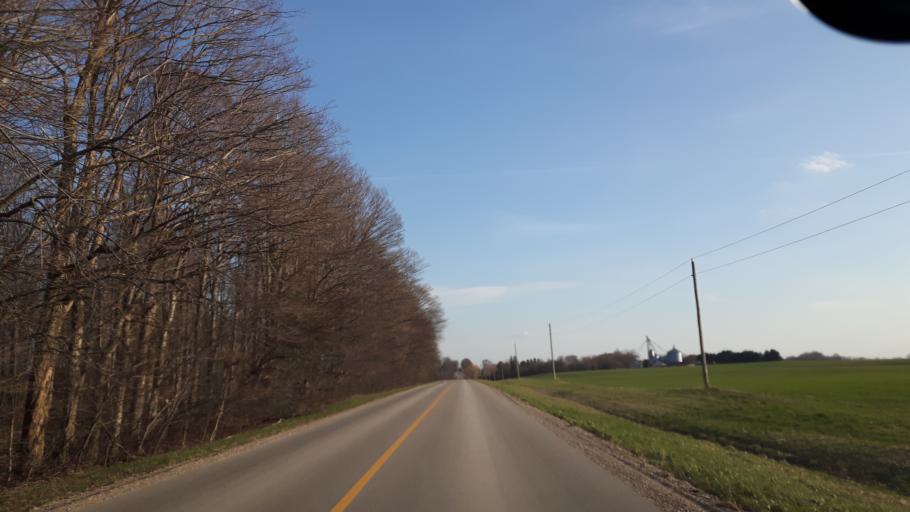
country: CA
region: Ontario
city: Goderich
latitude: 43.6498
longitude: -81.6643
